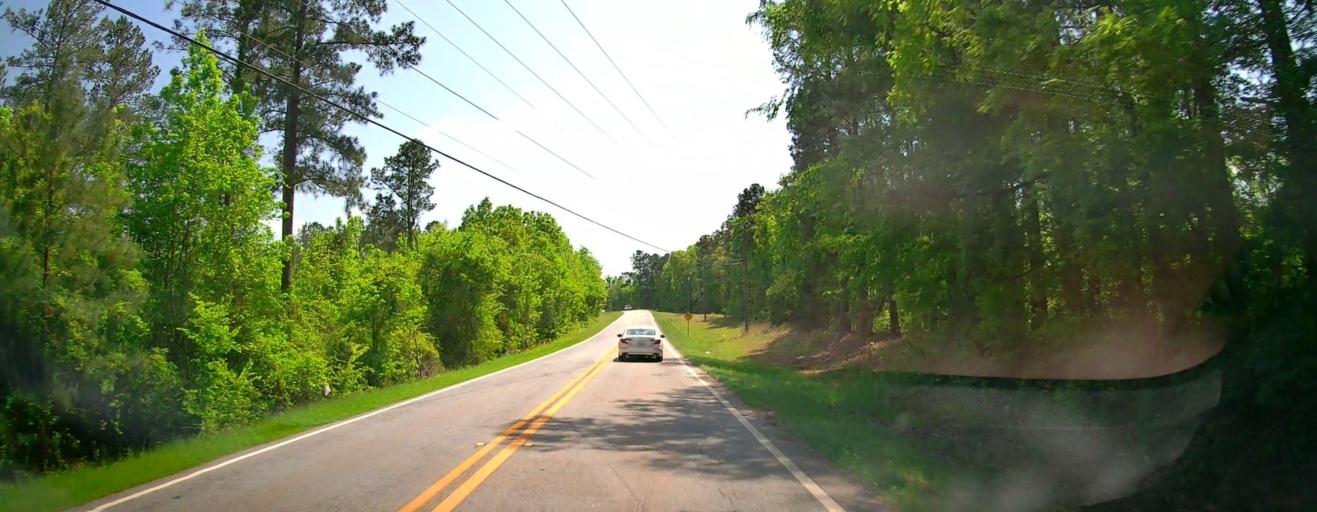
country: US
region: Georgia
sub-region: Putnam County
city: Eatonton
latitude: 33.2853
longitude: -83.3028
